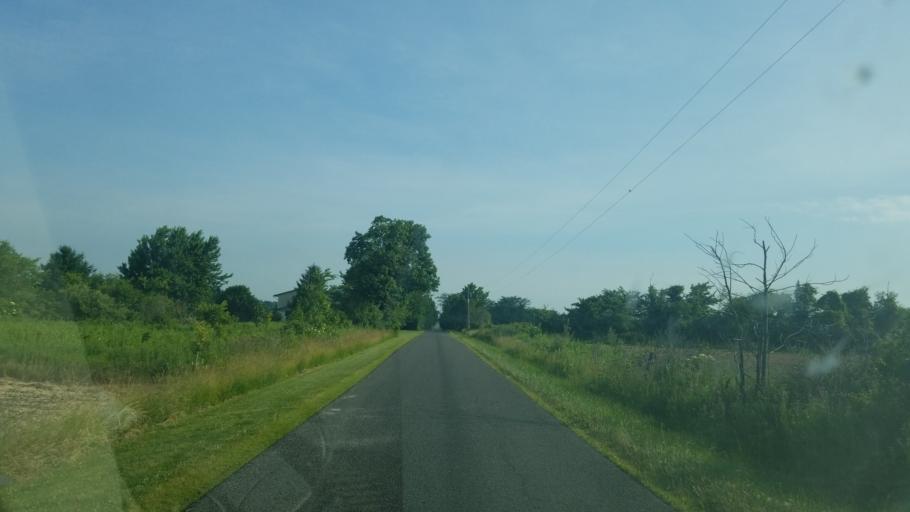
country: US
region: Ohio
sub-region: Hancock County
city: Arlington
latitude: 40.8497
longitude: -83.6702
